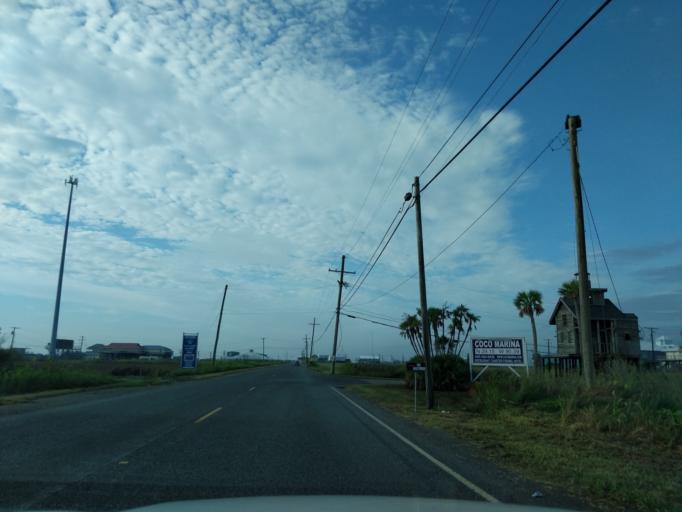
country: US
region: Louisiana
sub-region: Terrebonne Parish
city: Dulac
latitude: 29.2509
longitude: -90.6608
